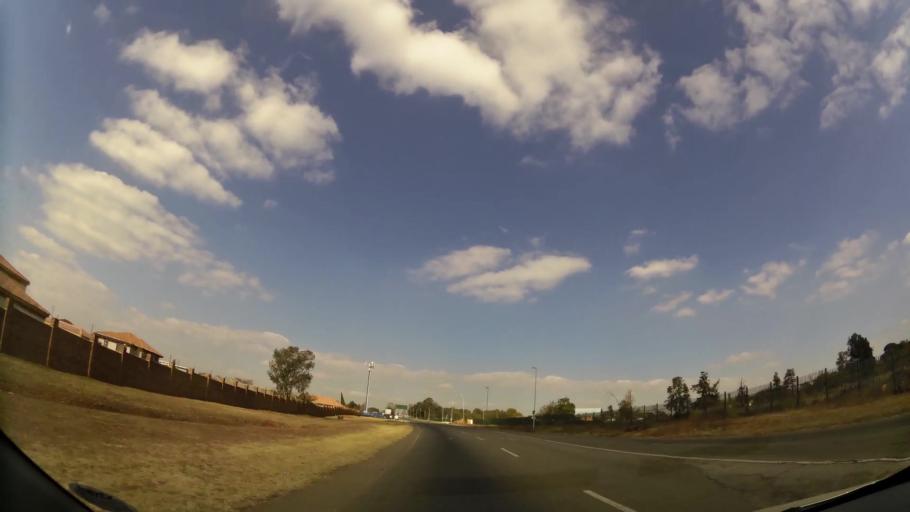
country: ZA
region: Gauteng
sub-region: West Rand District Municipality
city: Krugersdorp
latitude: -26.0574
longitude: 27.7552
